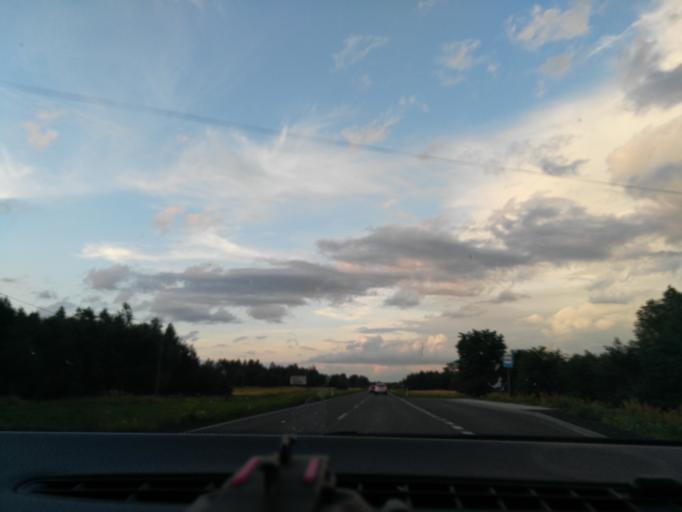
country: PL
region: Lublin Voivodeship
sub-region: Powiat lubartowski
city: Kock
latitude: 51.6712
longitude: 22.4782
